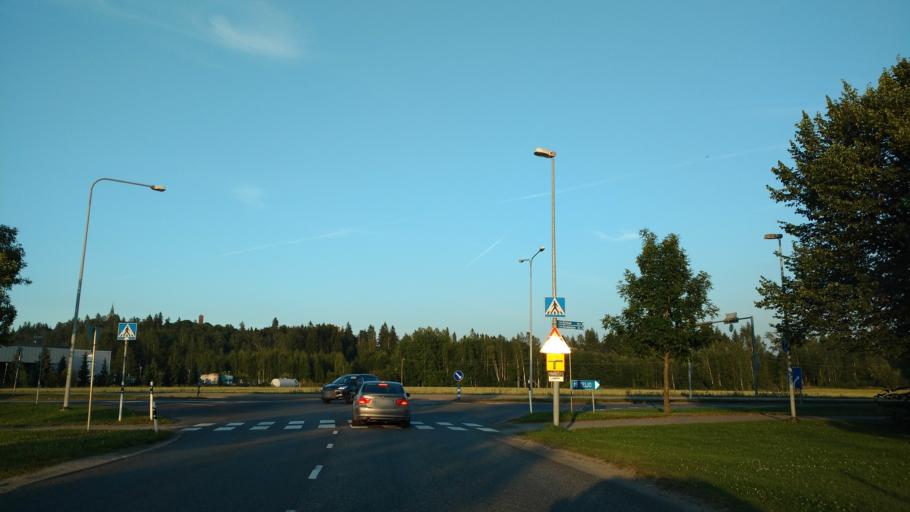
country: FI
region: Varsinais-Suomi
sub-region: Salo
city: Salo
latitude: 60.3751
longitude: 23.1151
